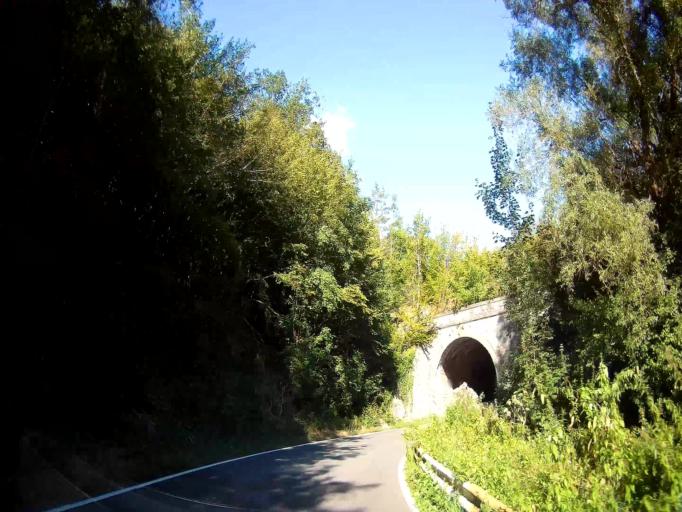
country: BE
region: Wallonia
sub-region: Province de Namur
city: Onhaye
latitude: 50.2952
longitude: 4.8138
